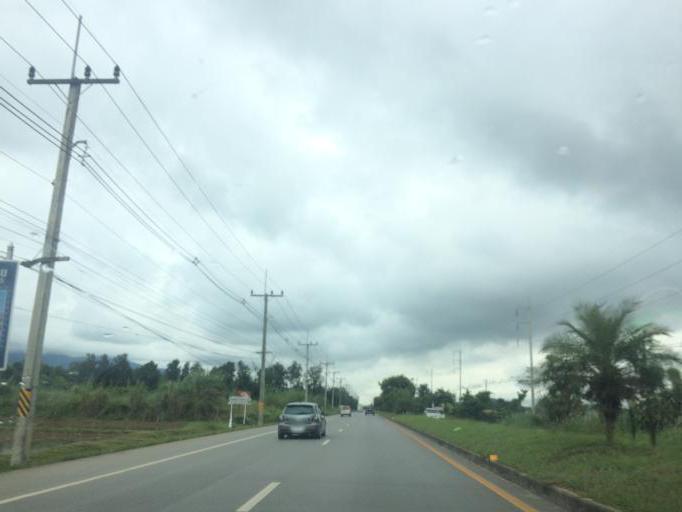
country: TH
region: Chiang Rai
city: Mae Chan
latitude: 20.0588
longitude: 99.8754
